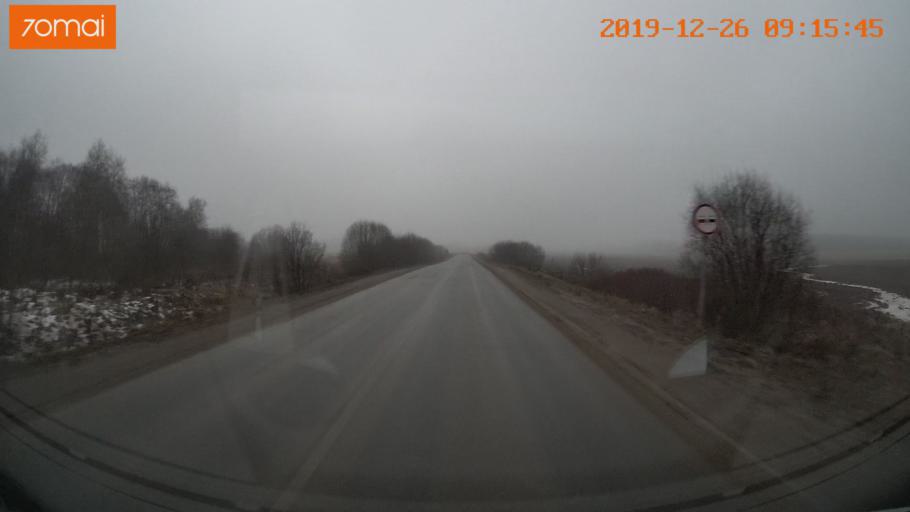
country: RU
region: Vologda
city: Gryazovets
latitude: 58.9091
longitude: 40.2397
